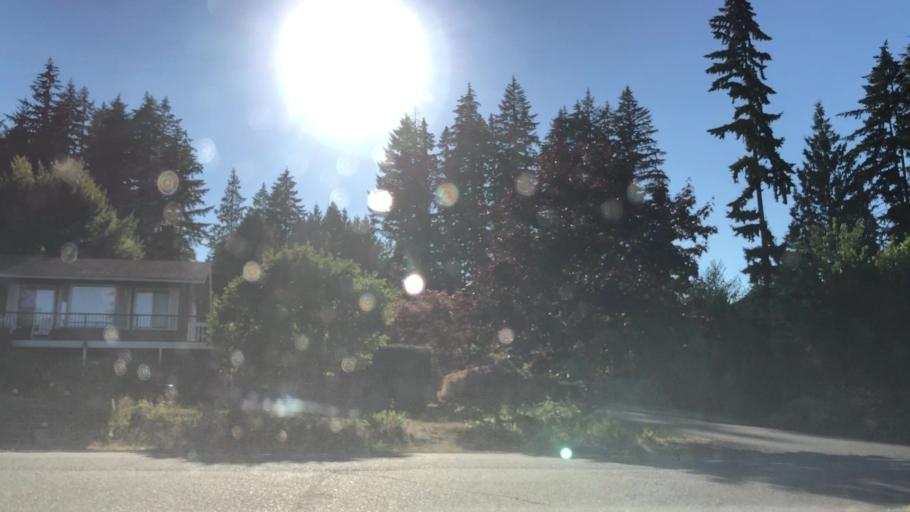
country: US
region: Washington
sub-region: King County
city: Bothell
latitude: 47.7948
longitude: -122.2273
